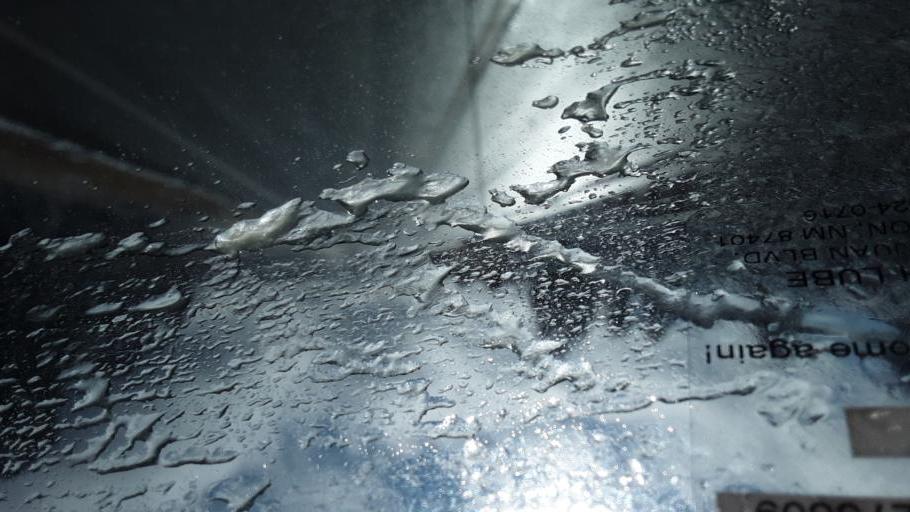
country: US
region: Colorado
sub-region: La Plata County
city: Bayfield
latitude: 37.2382
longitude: -107.5784
